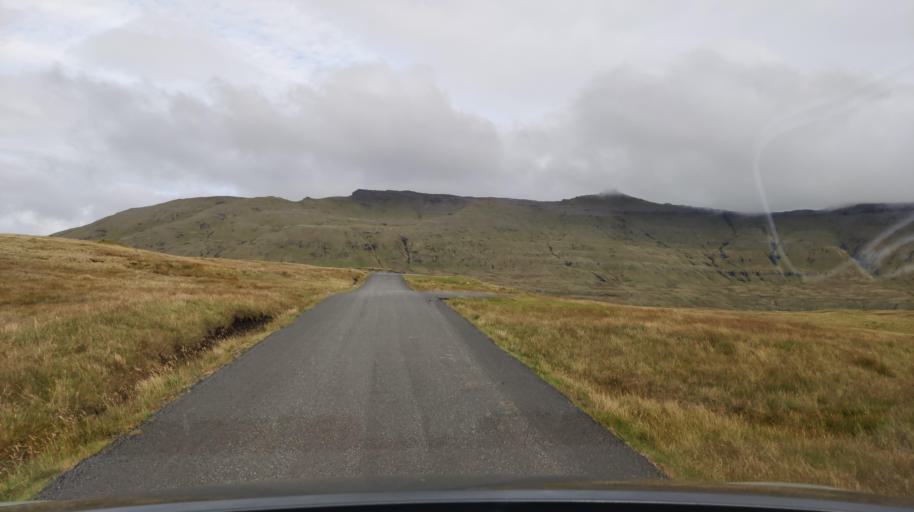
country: FO
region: Streymoy
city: Vestmanna
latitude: 62.1614
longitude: -7.0985
